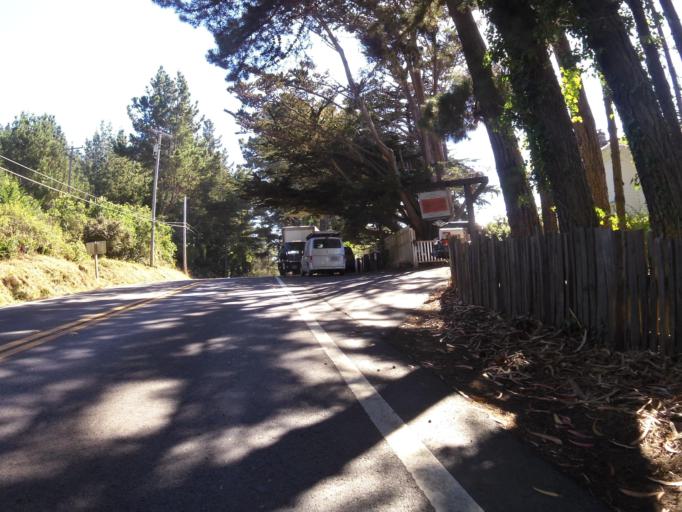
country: US
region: California
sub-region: Mendocino County
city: Fort Bragg
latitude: 39.6342
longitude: -123.7828
